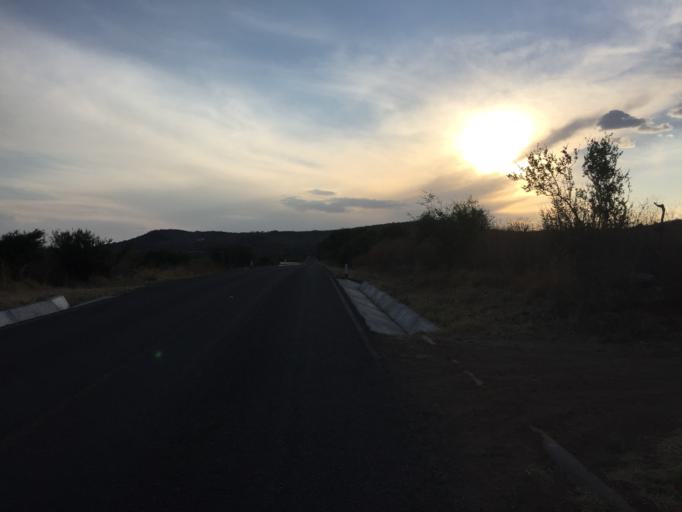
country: MX
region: Aguascalientes
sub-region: Aguascalientes
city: Pocitos
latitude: 21.9132
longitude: -102.3934
